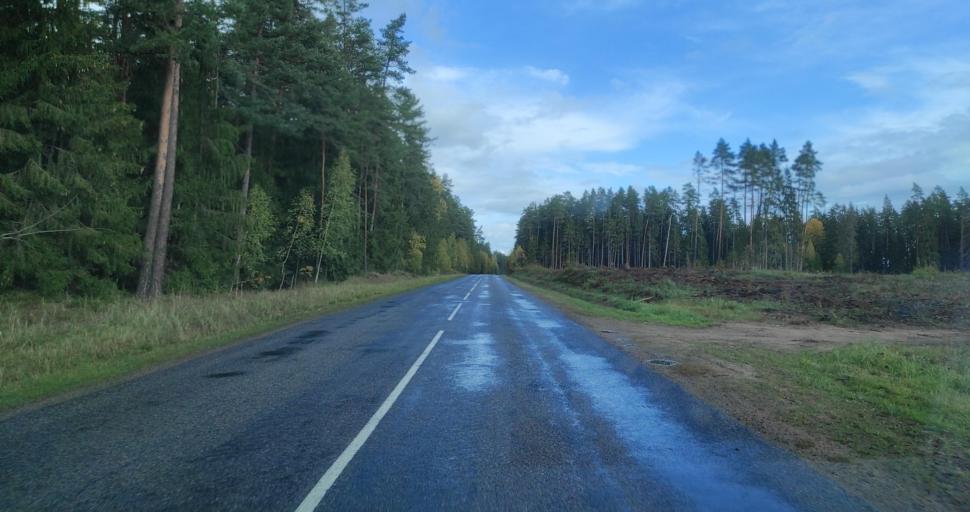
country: LV
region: Skrunda
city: Skrunda
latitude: 56.6377
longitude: 22.0065
